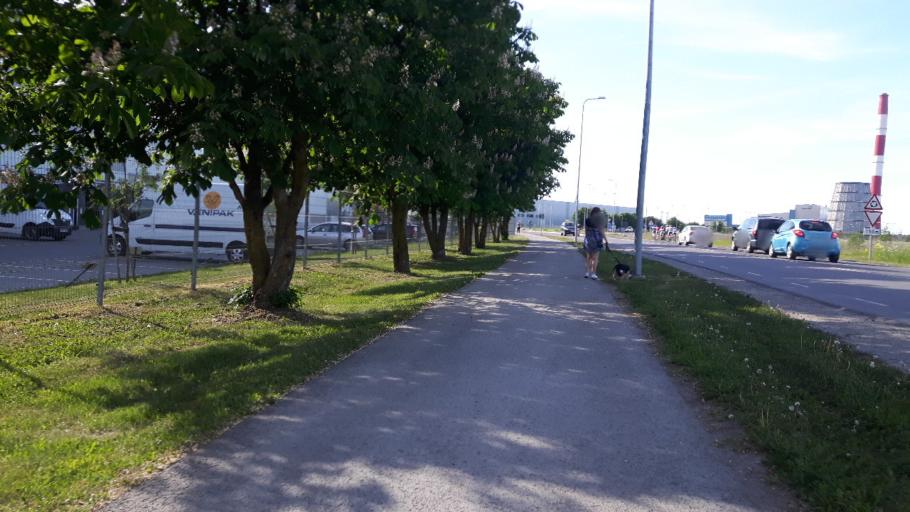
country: EE
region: Harju
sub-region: Joelaehtme vald
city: Loo
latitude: 59.4419
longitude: 24.9323
